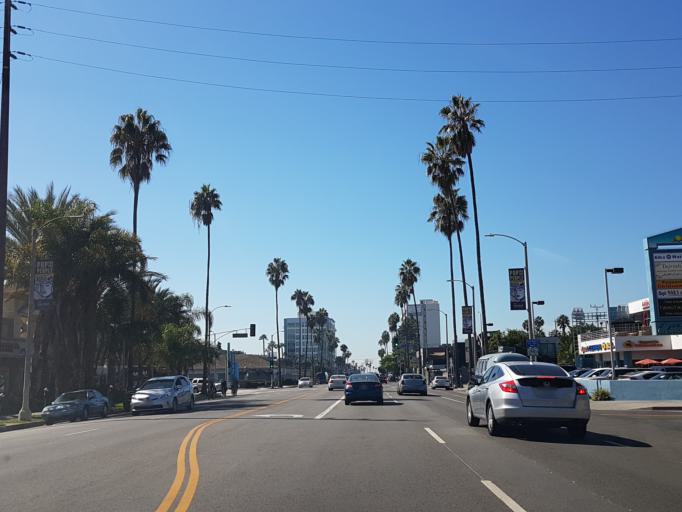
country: US
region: California
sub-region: Los Angeles County
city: Marina del Rey
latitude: 33.9831
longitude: -118.4602
